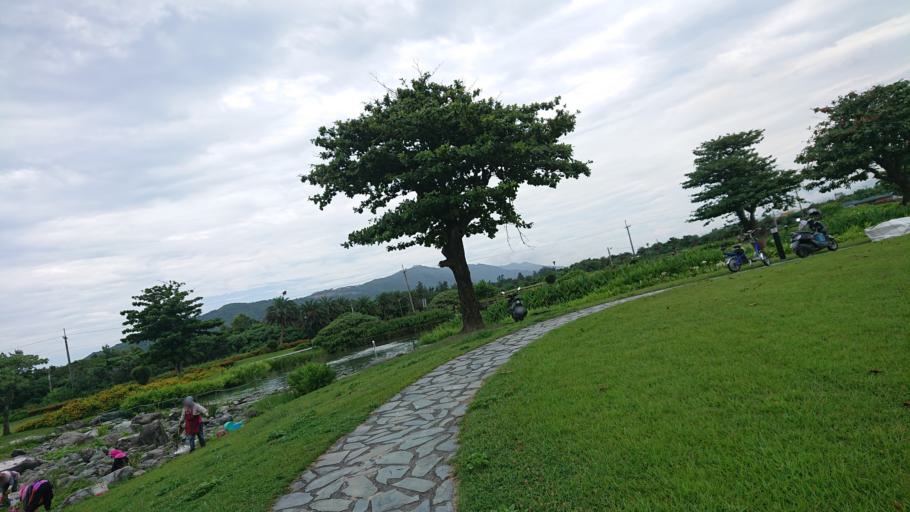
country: TW
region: Taiwan
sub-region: Hualien
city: Hualian
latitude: 23.9380
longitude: 121.6007
